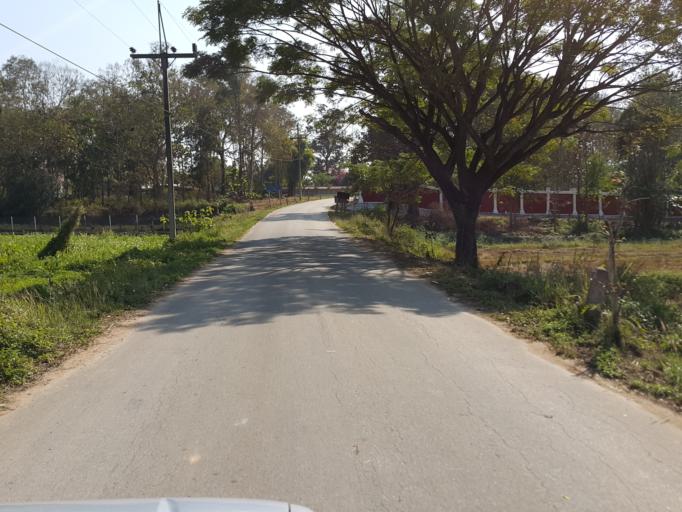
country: TH
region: Lampang
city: Wang Nuea
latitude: 19.0431
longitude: 99.6242
